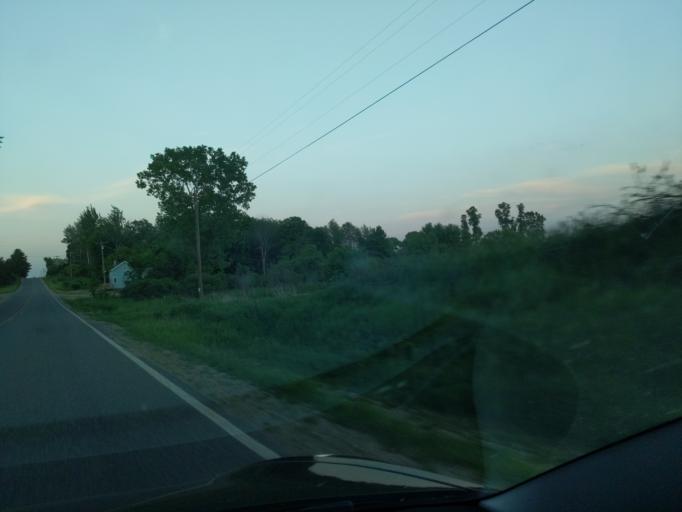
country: US
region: Michigan
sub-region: Barry County
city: Nashville
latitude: 42.5380
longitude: -85.0856
